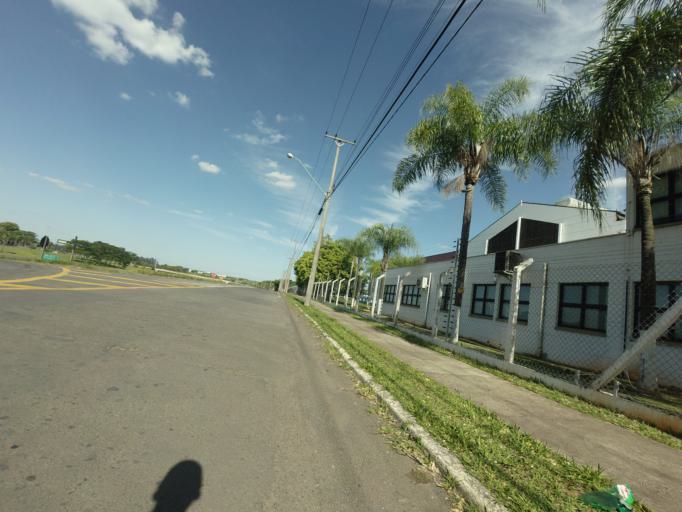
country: BR
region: Sao Paulo
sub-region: Piracicaba
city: Piracicaba
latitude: -22.7233
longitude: -47.5978
